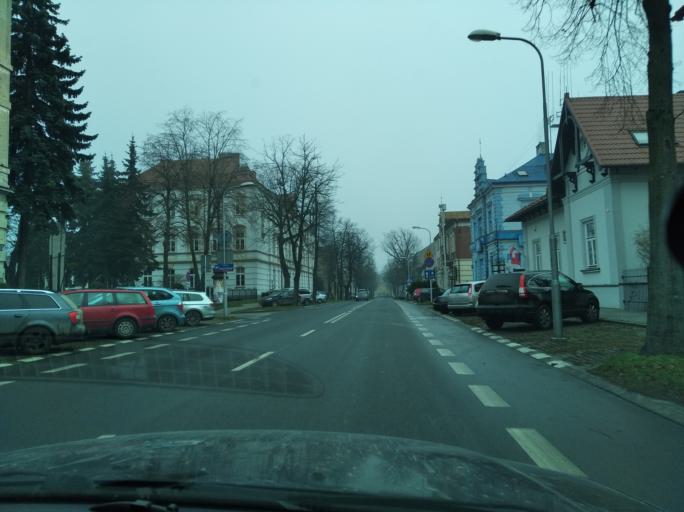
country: PL
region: Subcarpathian Voivodeship
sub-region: Rzeszow
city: Rzeszow
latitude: 50.0412
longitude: 21.9930
